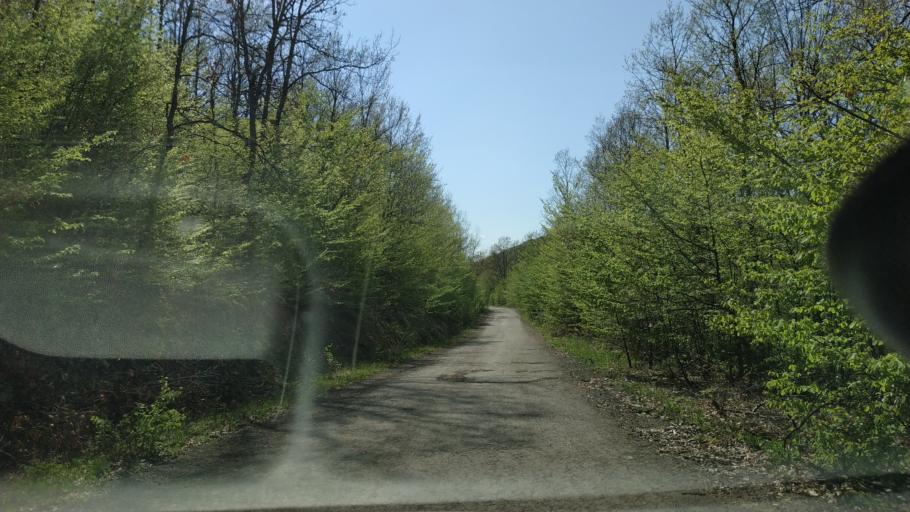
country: RS
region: Central Serbia
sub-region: Zajecarski Okrug
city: Soko Banja
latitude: 43.5054
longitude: 21.8949
